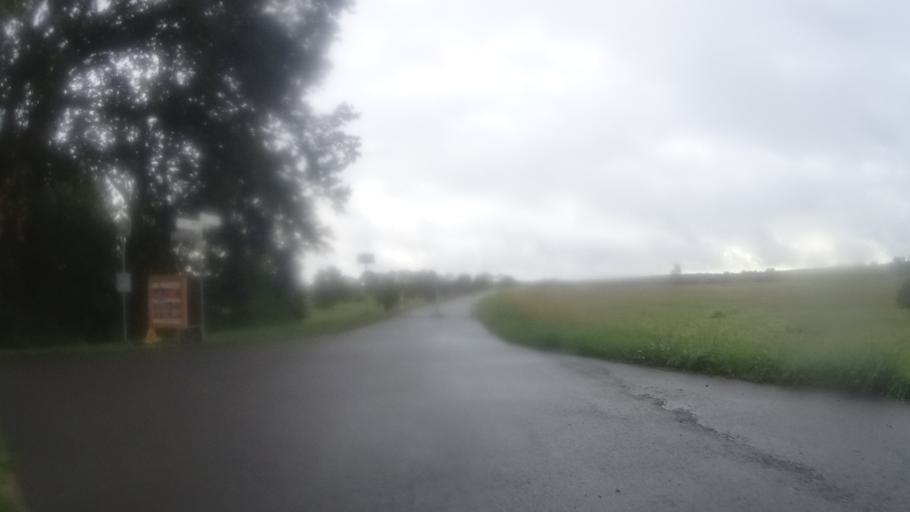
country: DE
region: Lower Saxony
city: Gorleben
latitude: 53.0636
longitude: 11.3372
